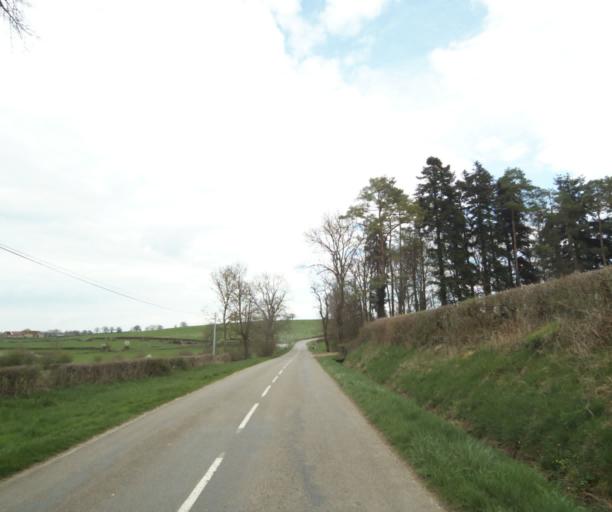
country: FR
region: Bourgogne
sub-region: Departement de Saone-et-Loire
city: Ciry-le-Noble
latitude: 46.5399
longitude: 4.3729
